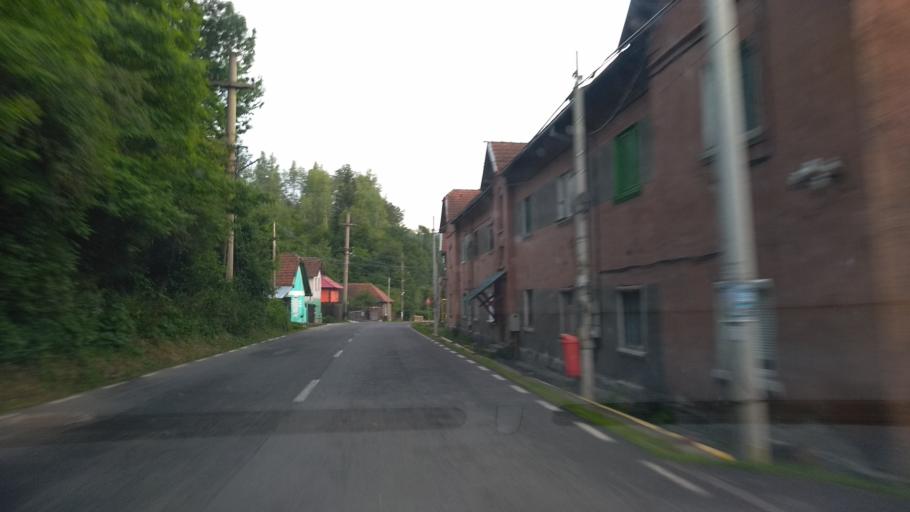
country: RO
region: Hunedoara
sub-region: Comuna Aninoasa
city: Aninoasa
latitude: 45.4005
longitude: 23.3203
